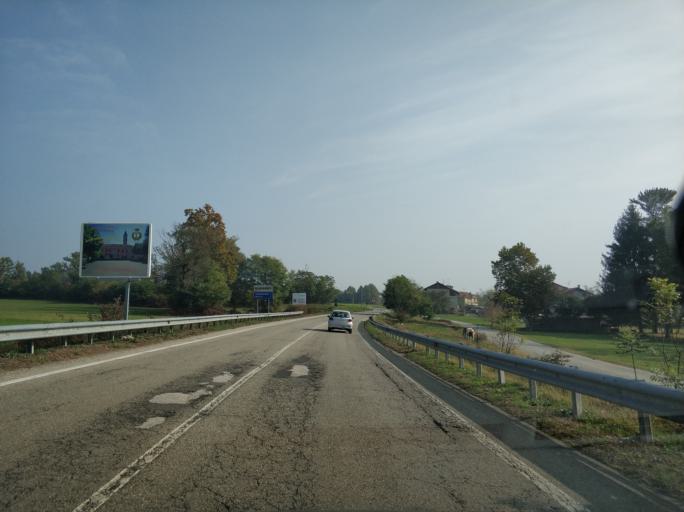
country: IT
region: Piedmont
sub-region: Provincia di Biella
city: Mongrando
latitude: 45.5285
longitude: 8.0251
